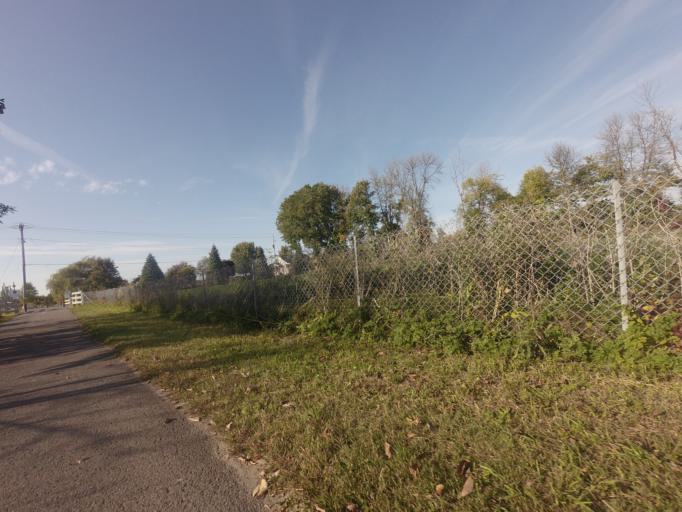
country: CA
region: Quebec
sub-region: Laurentides
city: Blainville
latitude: 45.7221
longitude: -73.9321
